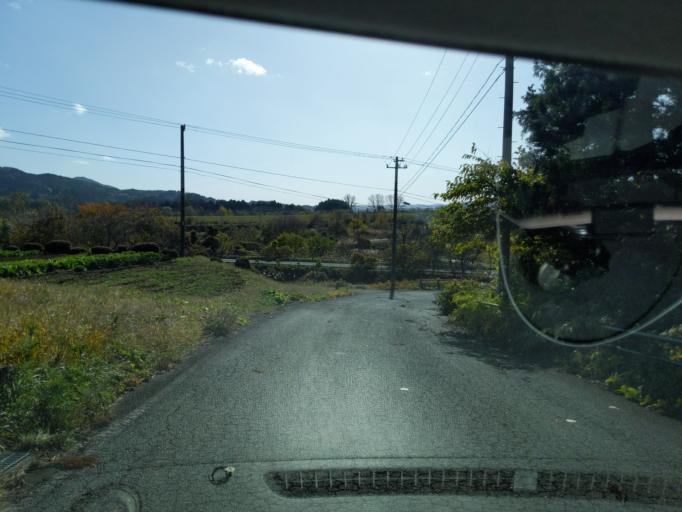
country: JP
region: Iwate
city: Ichinoseki
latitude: 39.0215
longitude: 141.1261
